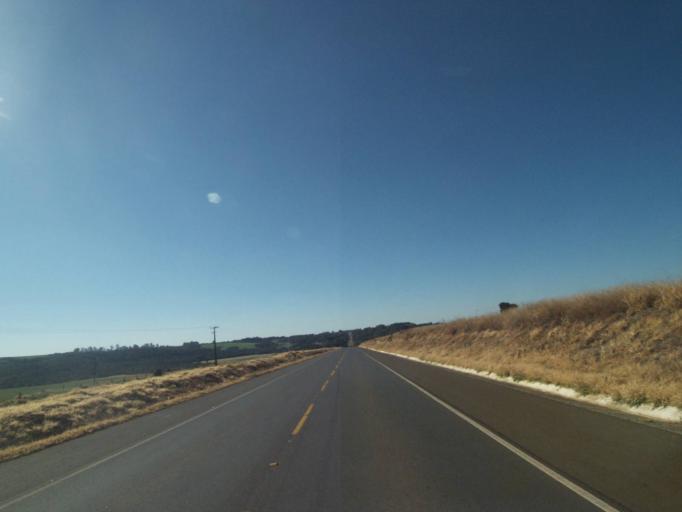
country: BR
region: Parana
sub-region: Tibagi
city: Tibagi
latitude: -24.6214
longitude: -50.4505
